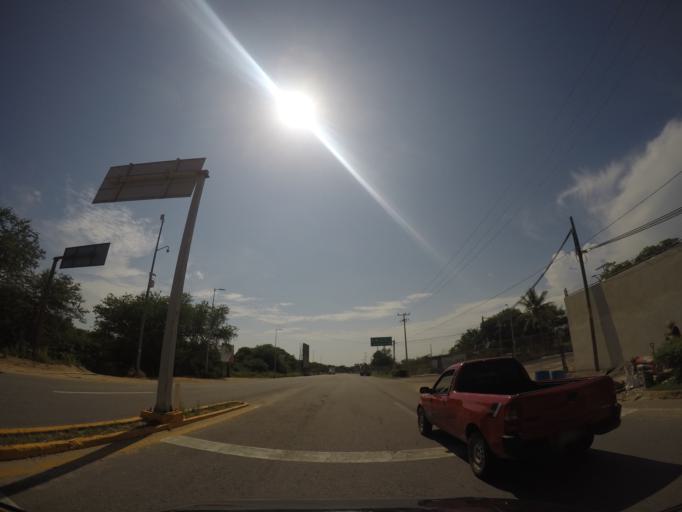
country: MX
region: Oaxaca
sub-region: San Pedro Mixtepec -Dto. 22 -
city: Puerto Escondido
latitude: 15.8719
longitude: -97.0918
